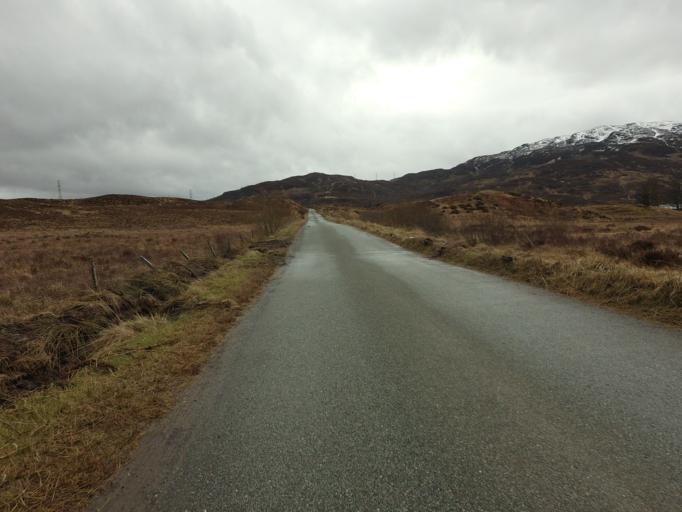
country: GB
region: Scotland
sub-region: West Dunbartonshire
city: Balloch
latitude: 56.2534
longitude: -4.5894
